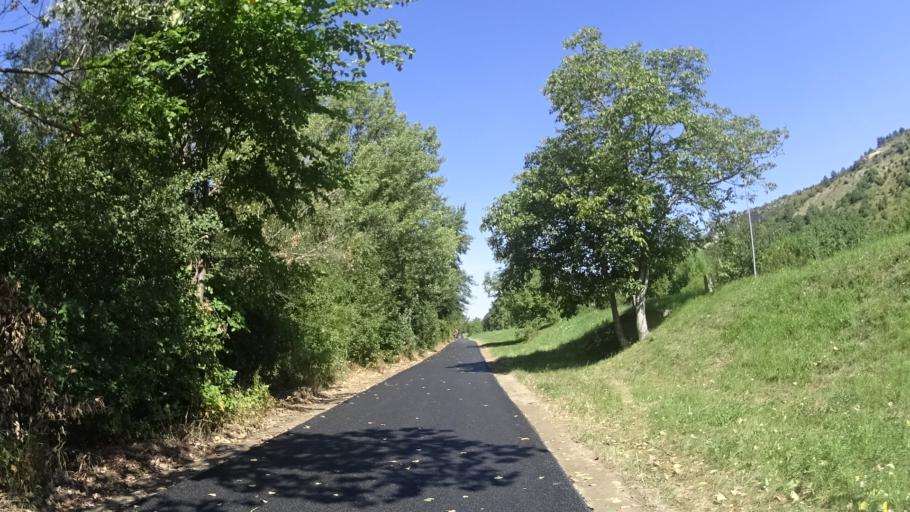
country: AT
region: Lower Austria
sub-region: Politischer Bezirk Bruck an der Leitha
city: Hainburg an der Donau
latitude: 48.1940
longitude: 16.9751
